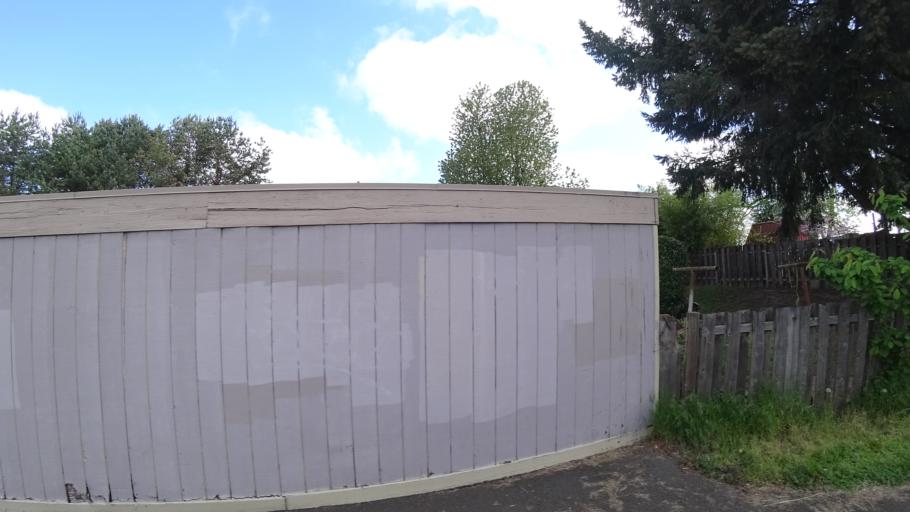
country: US
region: Oregon
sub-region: Washington County
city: Hillsboro
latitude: 45.5158
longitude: -122.9875
